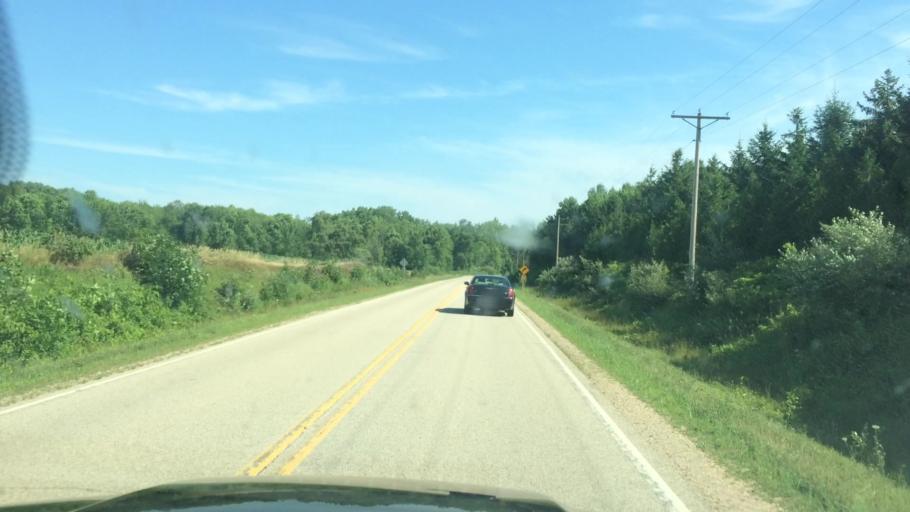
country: US
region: Wisconsin
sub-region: Oconto County
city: Gillett
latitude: 44.7904
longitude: -88.3119
